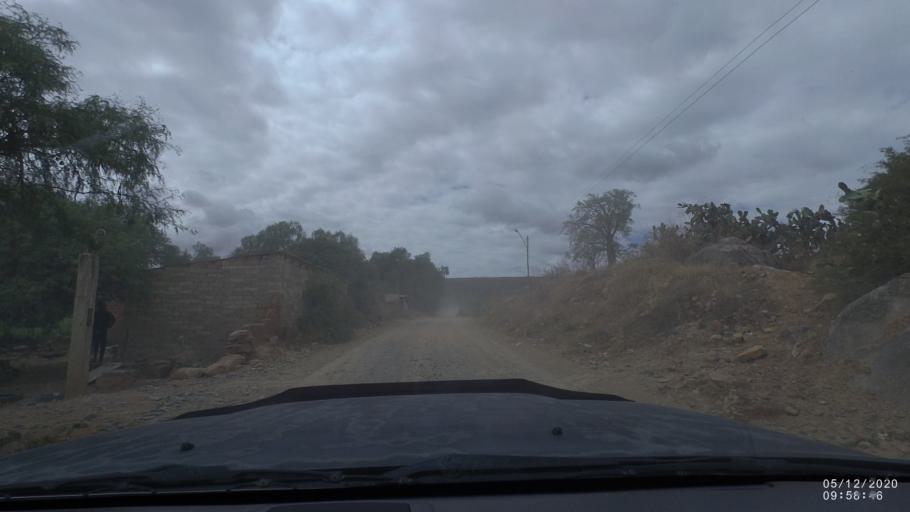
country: BO
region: Cochabamba
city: Sipe Sipe
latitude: -17.4311
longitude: -66.2921
